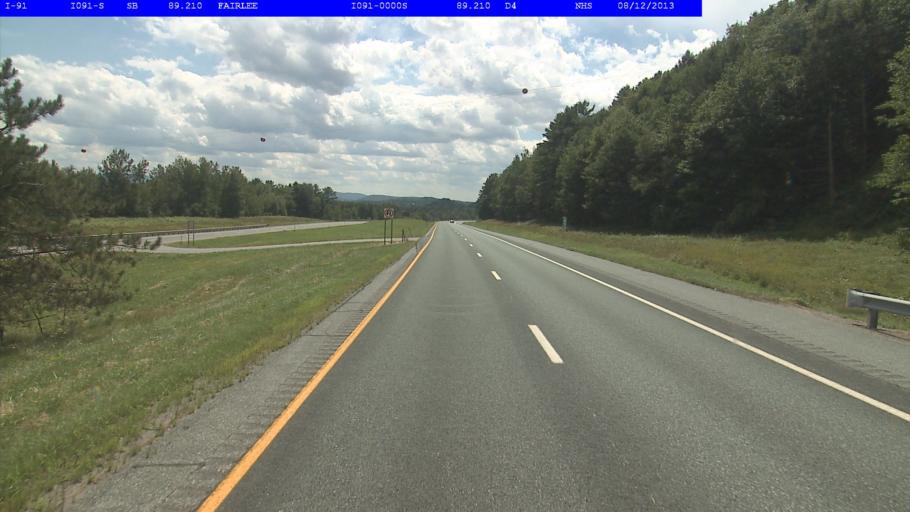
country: US
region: New Hampshire
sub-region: Grafton County
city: Orford
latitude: 43.8800
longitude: -72.1803
